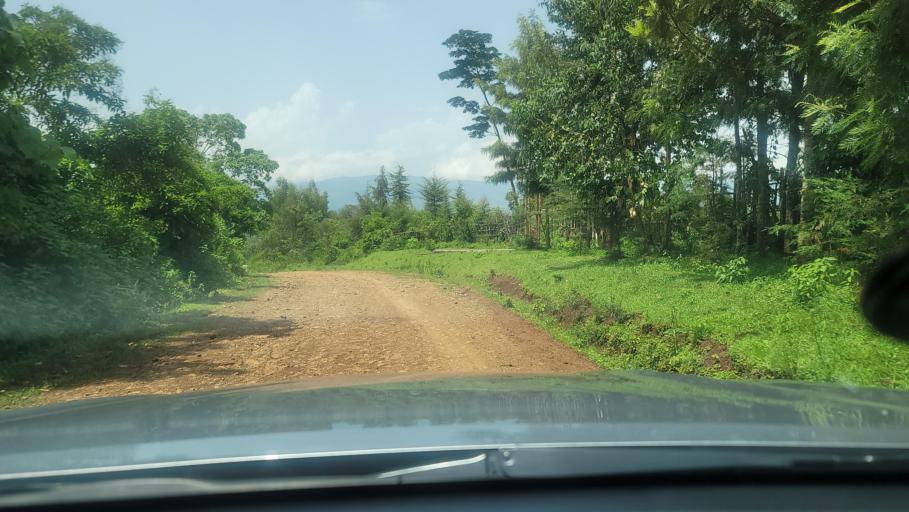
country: ET
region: Oromiya
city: Agaro
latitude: 7.8027
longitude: 36.4167
